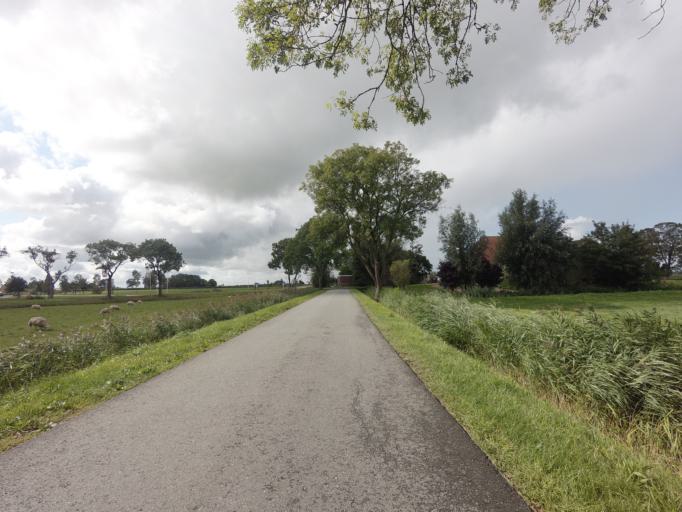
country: NL
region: Friesland
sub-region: Gemeente Boarnsterhim
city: Wergea
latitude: 53.1517
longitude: 5.8383
